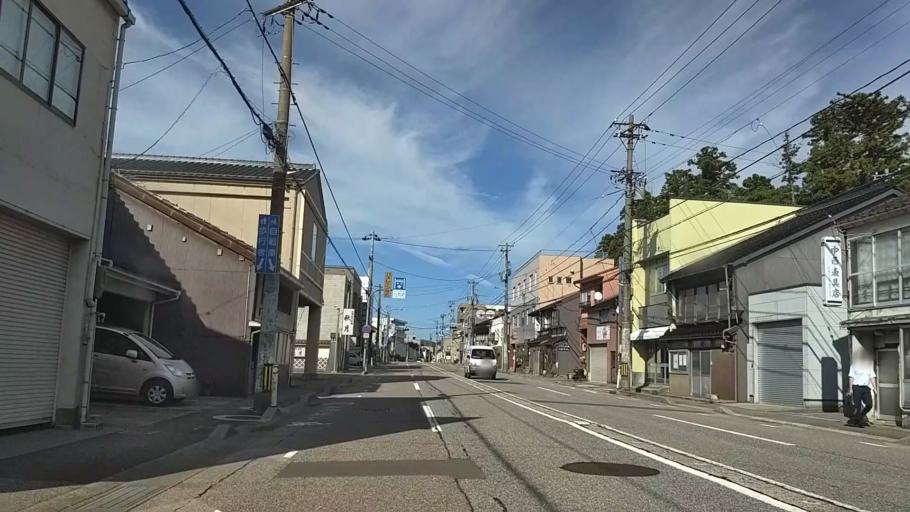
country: JP
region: Ishikawa
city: Kanazawa-shi
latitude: 36.5758
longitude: 136.6673
